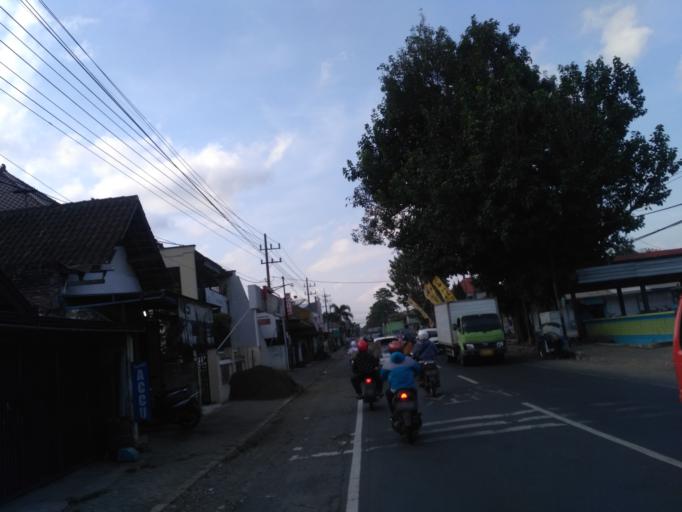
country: ID
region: East Java
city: Pakisaji
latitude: -8.0649
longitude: 112.5992
